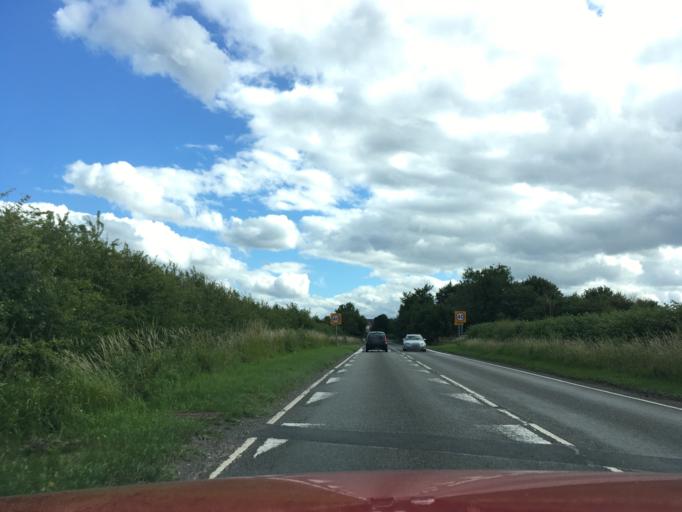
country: GB
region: England
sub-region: Leicestershire
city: Donisthorpe
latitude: 52.6808
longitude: -1.5452
